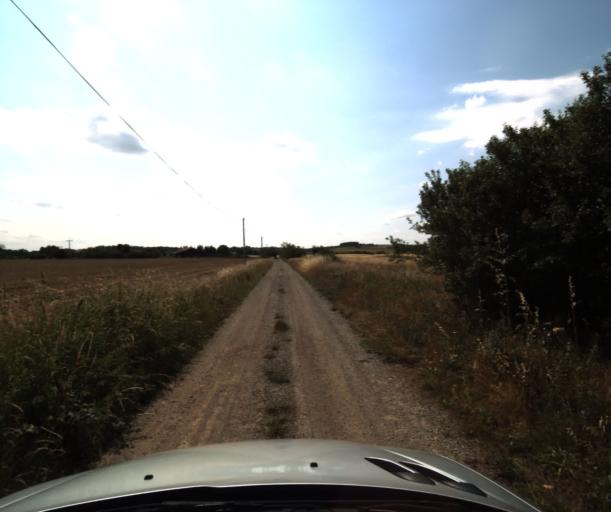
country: FR
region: Midi-Pyrenees
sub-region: Departement de la Haute-Garonne
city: Saint-Lys
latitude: 43.5089
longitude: 1.1637
